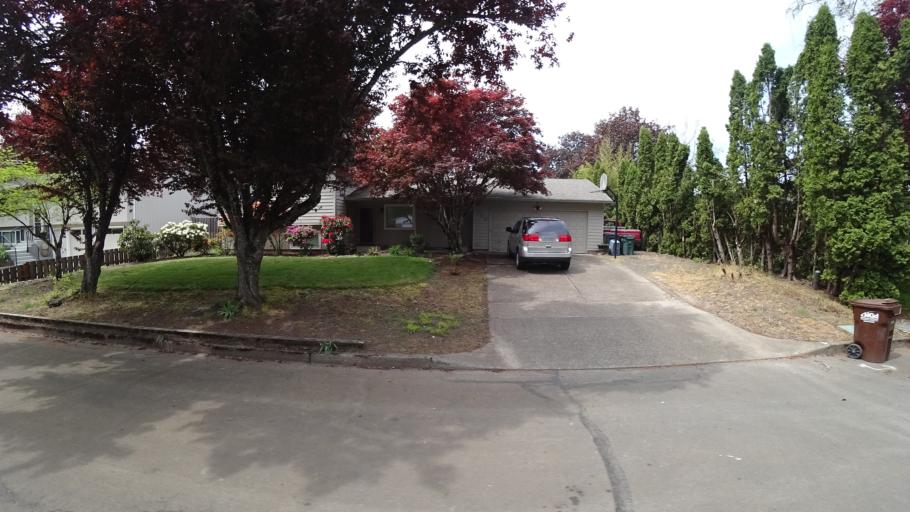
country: US
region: Oregon
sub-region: Washington County
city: Hillsboro
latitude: 45.5141
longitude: -122.9445
